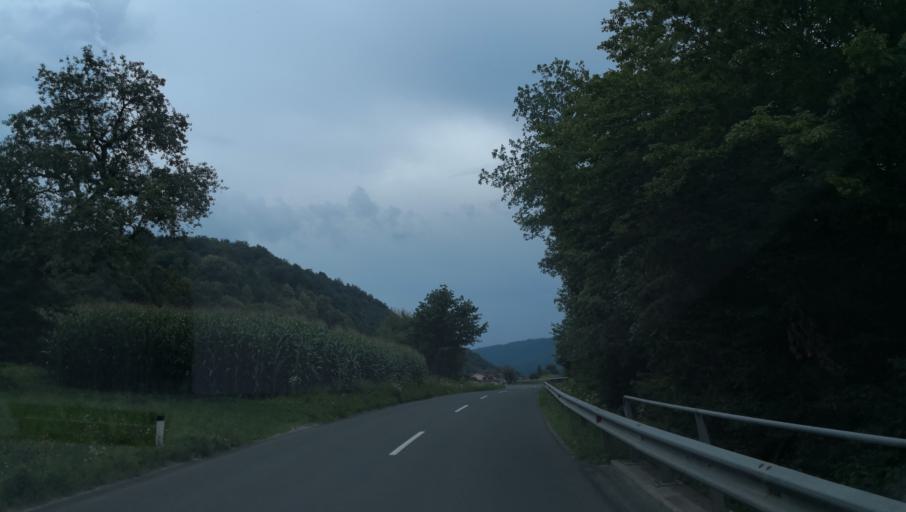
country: SI
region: Zuzemberk
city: Zuzemberk
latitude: 45.8155
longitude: 14.9617
